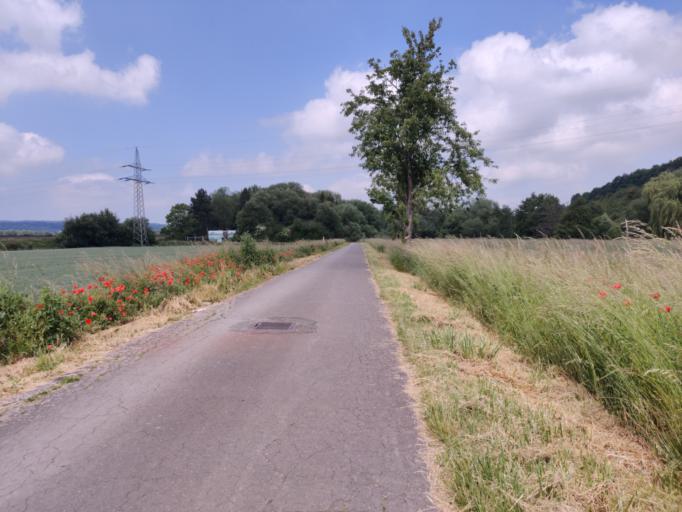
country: DE
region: Lower Saxony
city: Hildesheim
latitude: 52.1235
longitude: 9.9695
